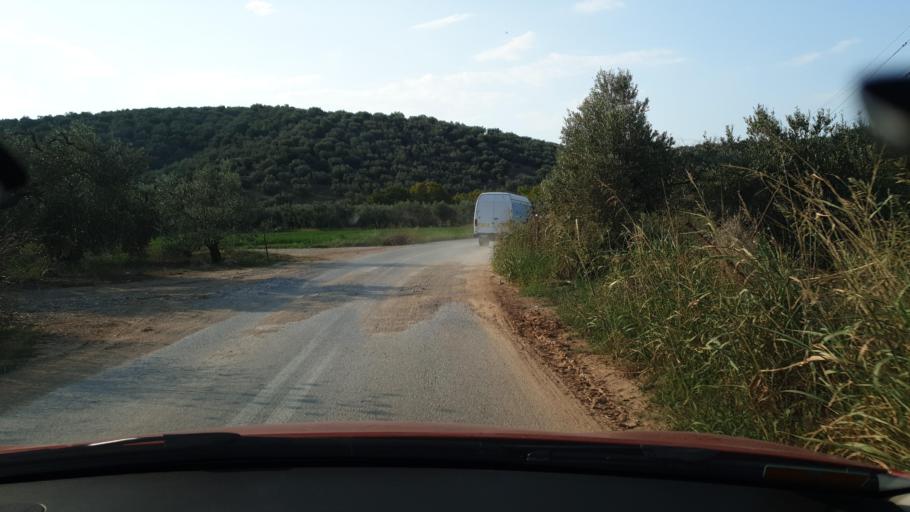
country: GR
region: Thessaly
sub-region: Nomos Magnisias
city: Pteleos
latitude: 38.9949
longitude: 22.9598
